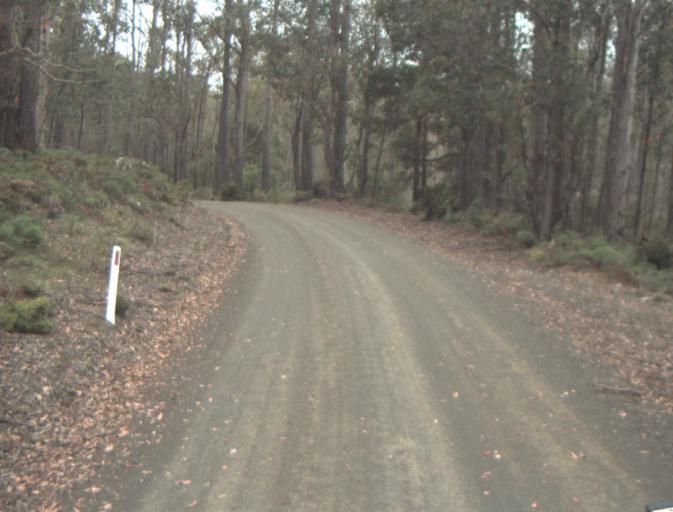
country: AU
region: Tasmania
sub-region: Northern Midlands
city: Evandale
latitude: -41.5000
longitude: 147.5845
